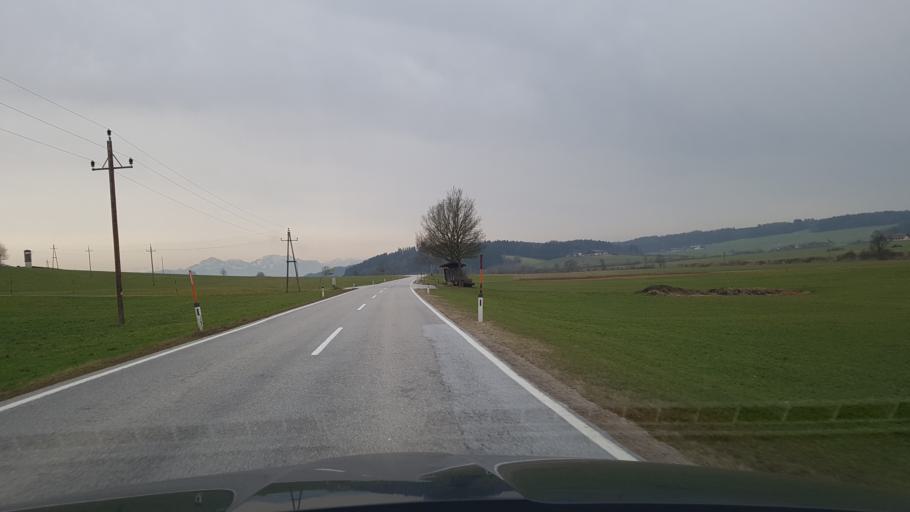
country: AT
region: Salzburg
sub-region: Politischer Bezirk Salzburg-Umgebung
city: Dorfbeuern
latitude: 47.9876
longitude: 13.0165
